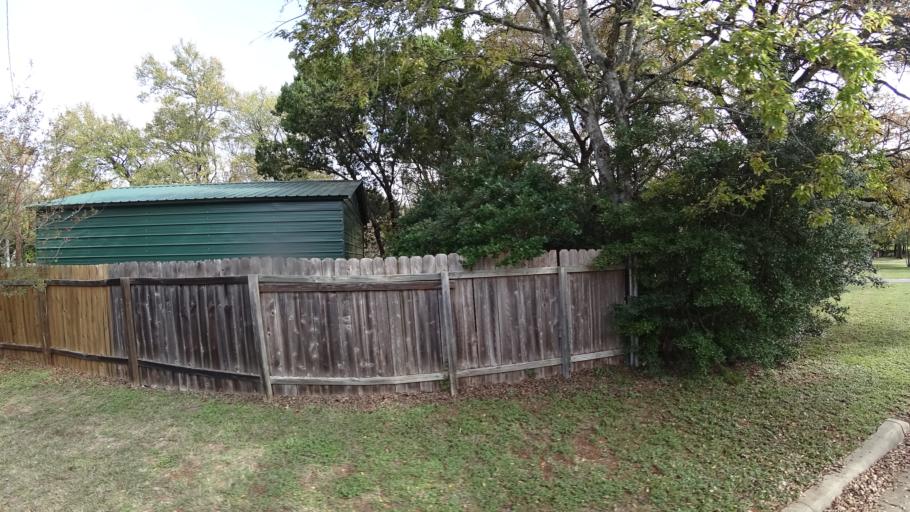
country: US
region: Texas
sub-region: Travis County
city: Wells Branch
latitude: 30.4332
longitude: -97.7123
